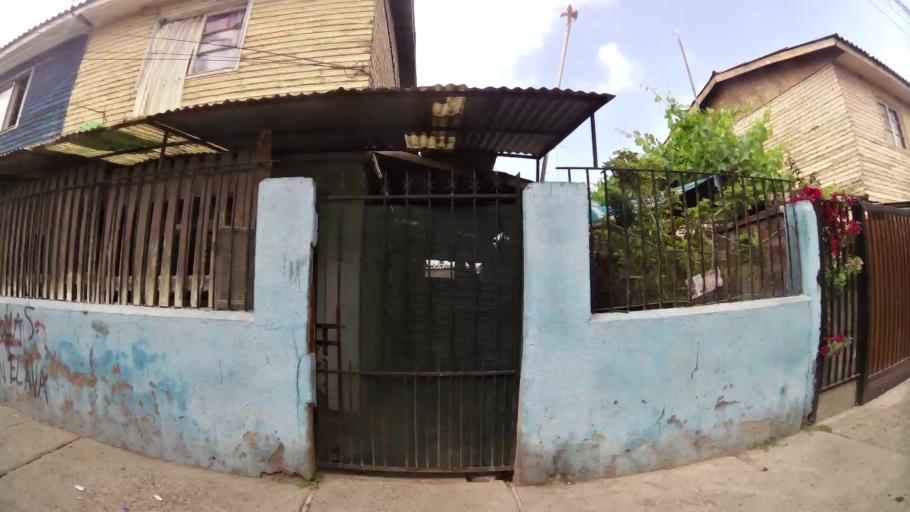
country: CL
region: Santiago Metropolitan
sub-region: Provincia de Santiago
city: Santiago
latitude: -33.5043
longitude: -70.6864
